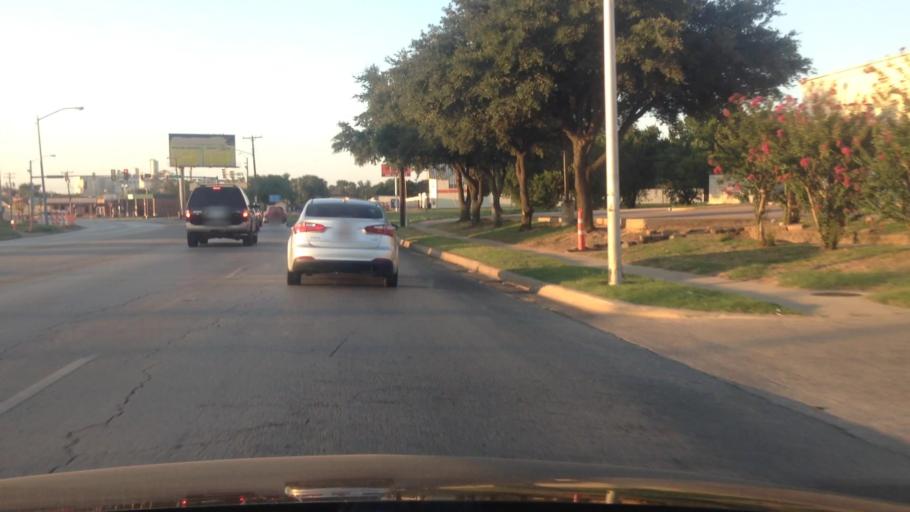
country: US
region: Texas
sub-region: Tarrant County
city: Haltom City
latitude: 32.7797
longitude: -97.2908
